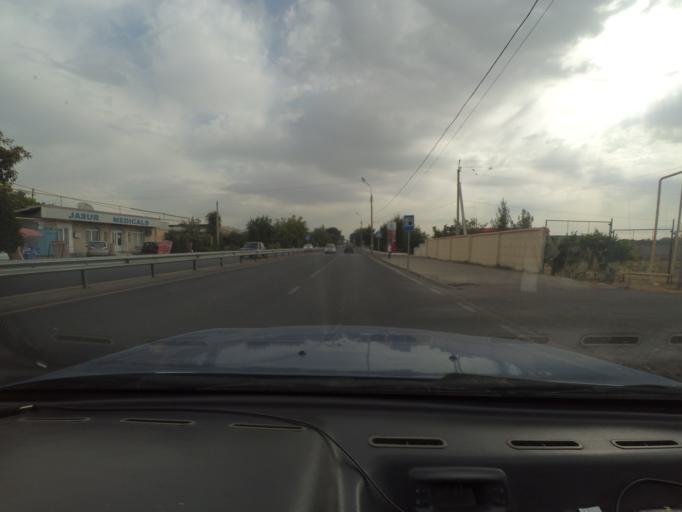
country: UZ
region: Toshkent
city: Qibray
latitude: 41.3734
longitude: 69.4289
